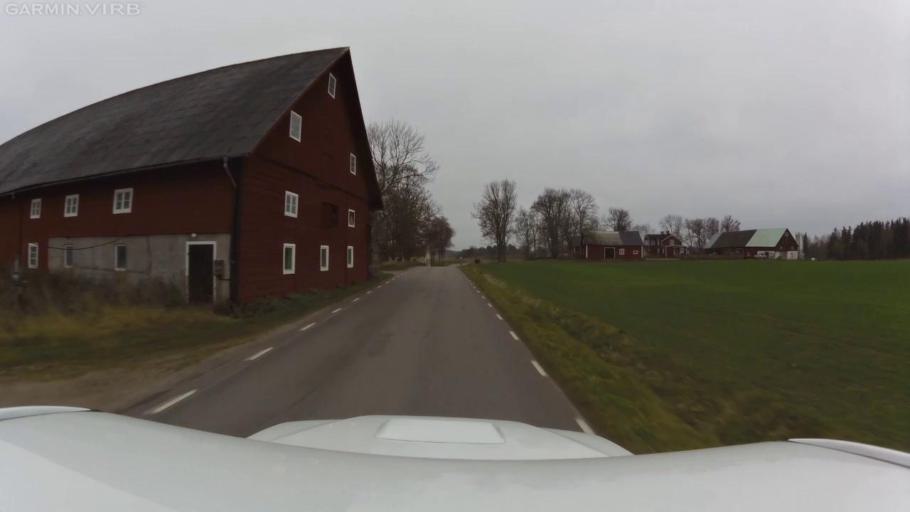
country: SE
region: OEstergoetland
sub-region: Linkopings Kommun
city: Vikingstad
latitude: 58.3090
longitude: 15.3811
